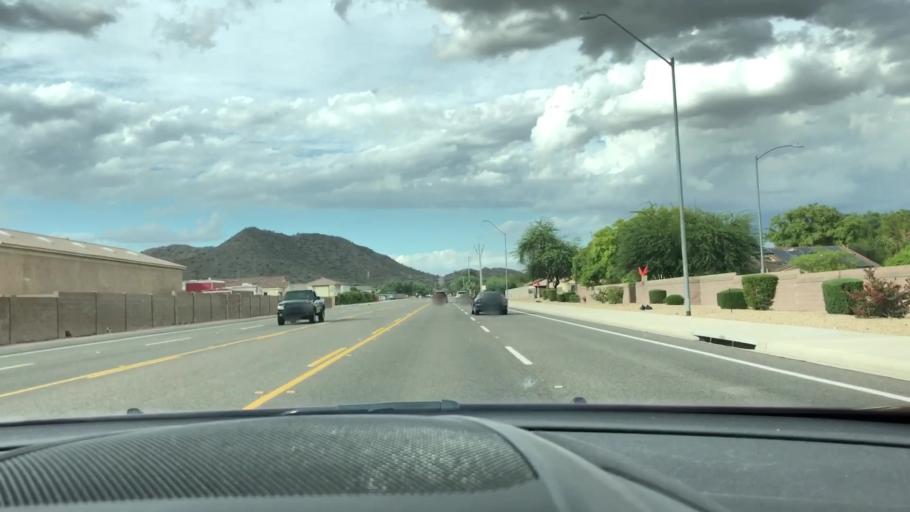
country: US
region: Arizona
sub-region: Maricopa County
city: Sun City
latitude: 33.6987
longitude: -112.2376
